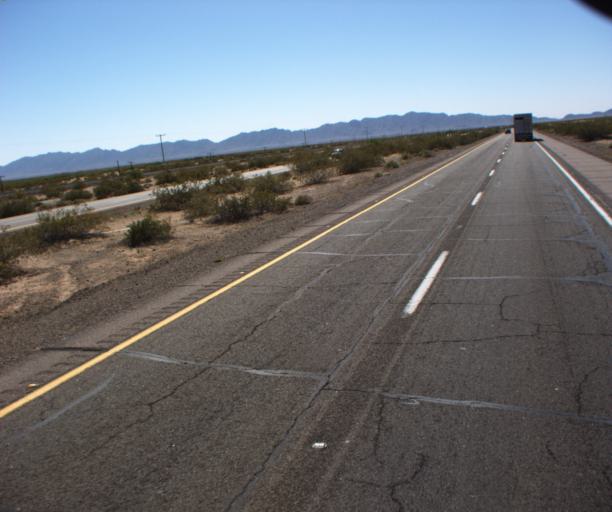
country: US
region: Arizona
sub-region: Yuma County
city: Wellton
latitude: 32.7784
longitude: -113.5895
